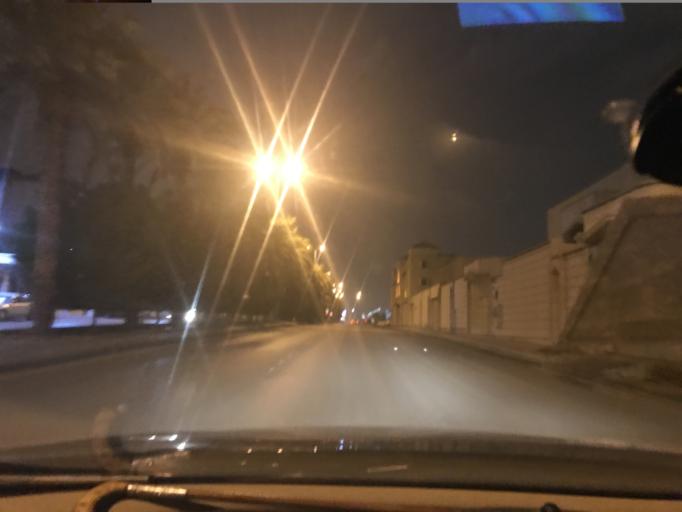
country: SA
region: Ar Riyad
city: Riyadh
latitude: 24.7176
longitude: 46.7747
